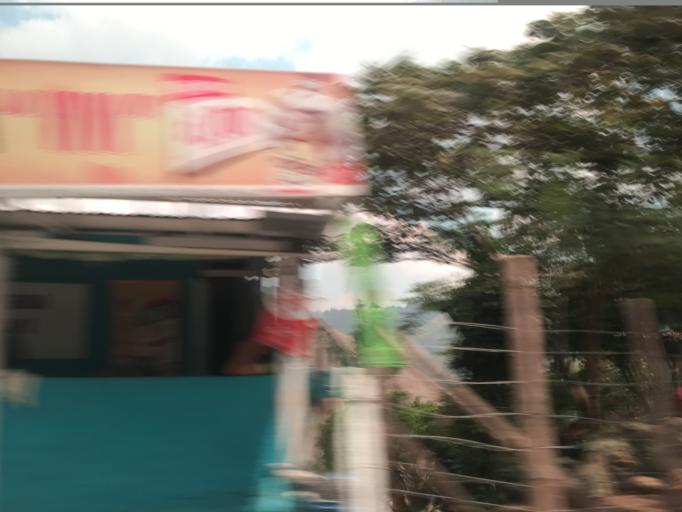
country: CO
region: Valle del Cauca
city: Cali
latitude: 3.4775
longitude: -76.5960
